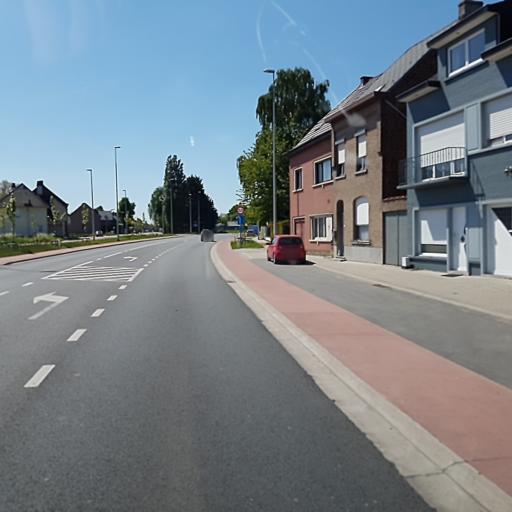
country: BE
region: Flanders
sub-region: Provincie Oost-Vlaanderen
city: Lede
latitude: 50.9407
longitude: 3.9904
